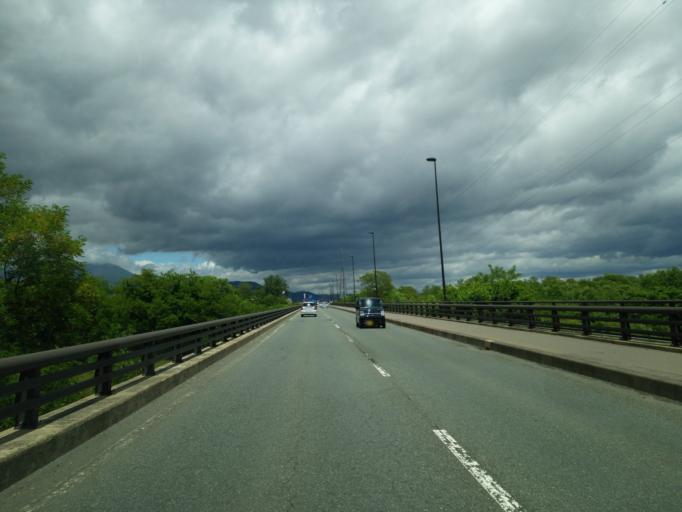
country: JP
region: Iwate
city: Morioka-shi
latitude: 39.7043
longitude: 141.1020
